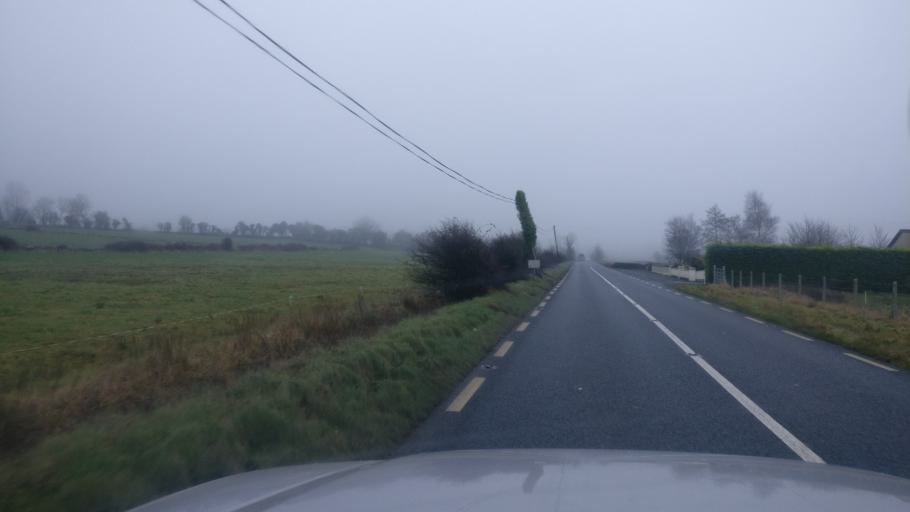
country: IE
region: Connaught
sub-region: County Galway
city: Loughrea
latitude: 53.1861
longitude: -8.6265
